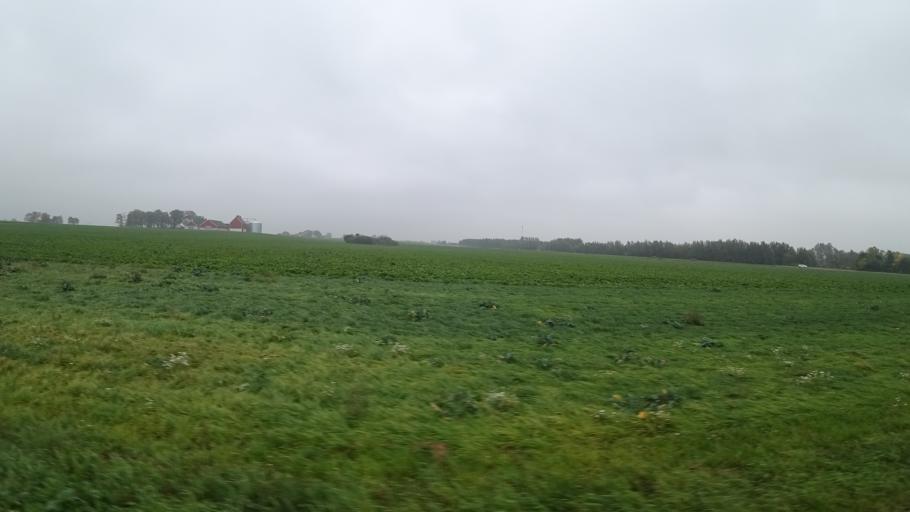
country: SE
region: Skane
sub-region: Kavlinge Kommun
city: Kaevlinge
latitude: 55.7992
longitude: 13.1503
